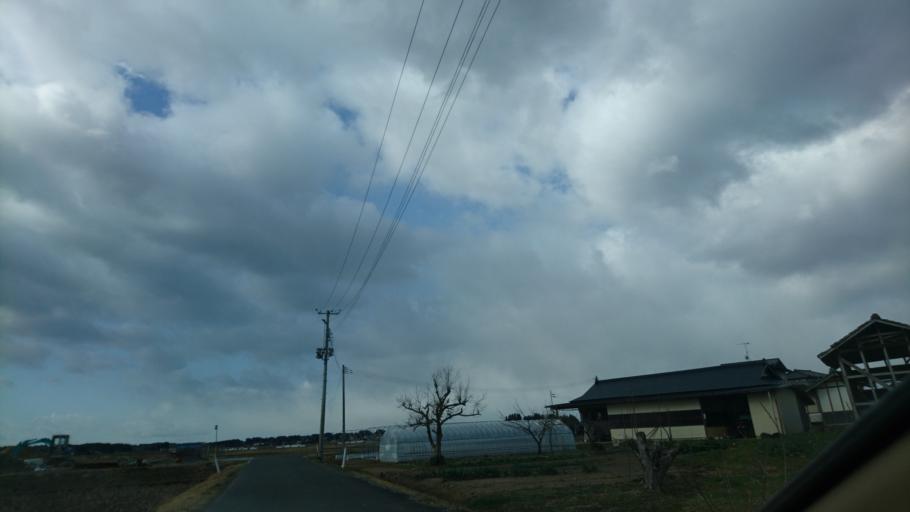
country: JP
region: Iwate
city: Ichinoseki
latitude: 38.7705
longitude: 141.1167
